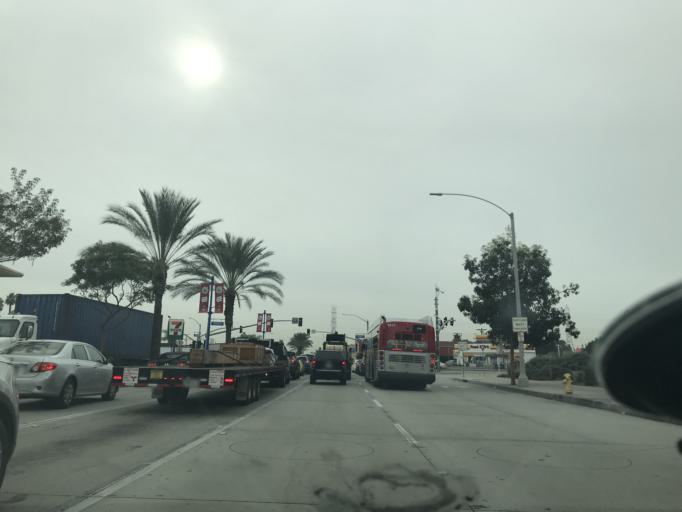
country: US
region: California
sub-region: Los Angeles County
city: Cudahy
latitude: 33.9528
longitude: -118.1835
